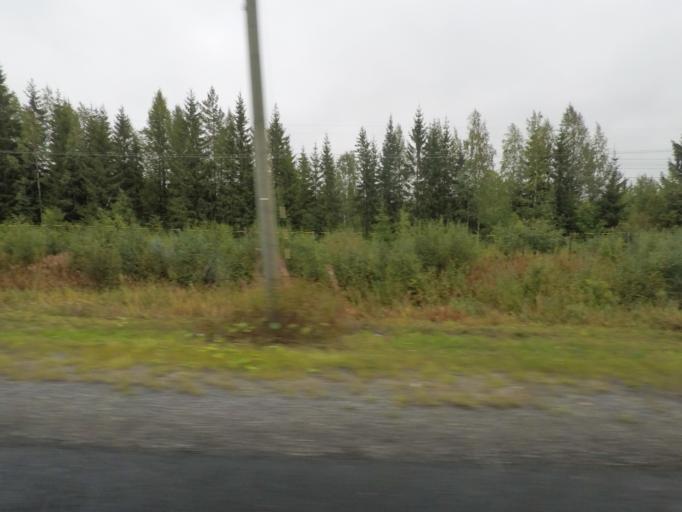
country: FI
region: Northern Savo
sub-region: Kuopio
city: Kuopio
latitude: 62.7831
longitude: 27.5932
